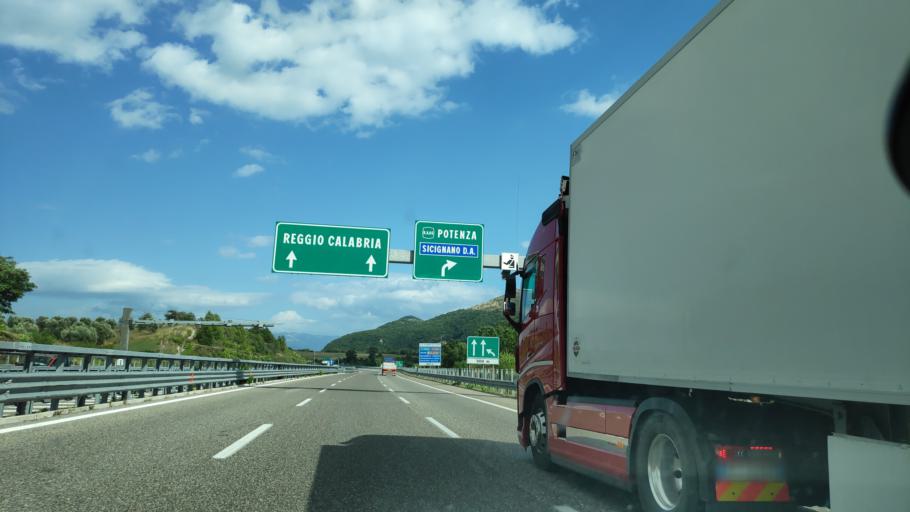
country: IT
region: Campania
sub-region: Provincia di Salerno
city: Palomonte
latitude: 40.6130
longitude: 15.2798
